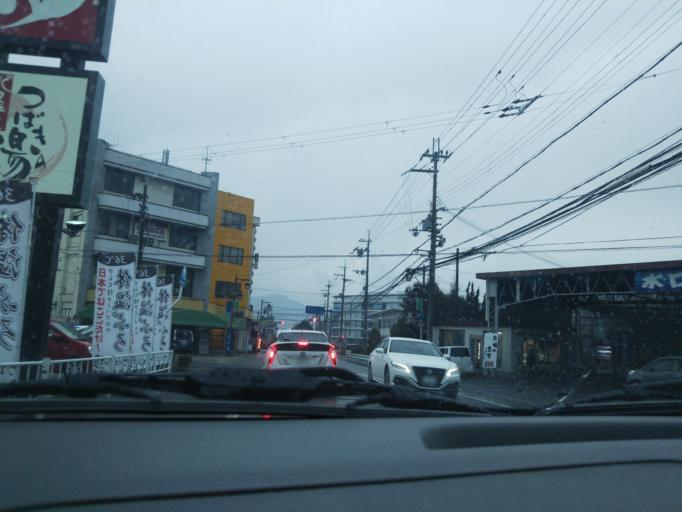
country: JP
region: Shiga Prefecture
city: Minakuchicho-matoba
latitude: 34.9659
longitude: 136.1694
